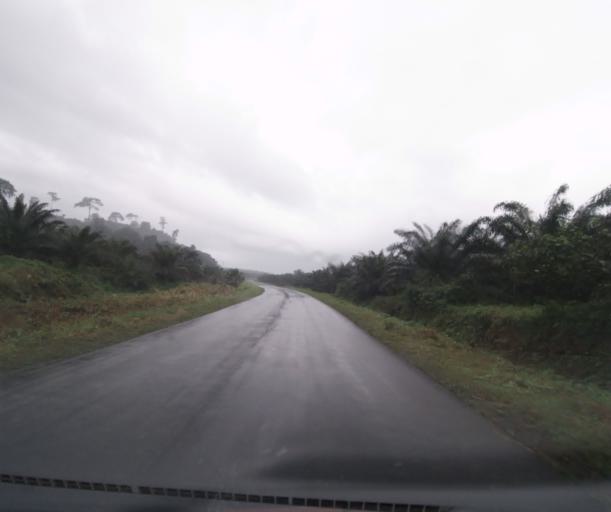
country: CM
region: South-West Province
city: Idenao
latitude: 4.1640
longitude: 8.9941
